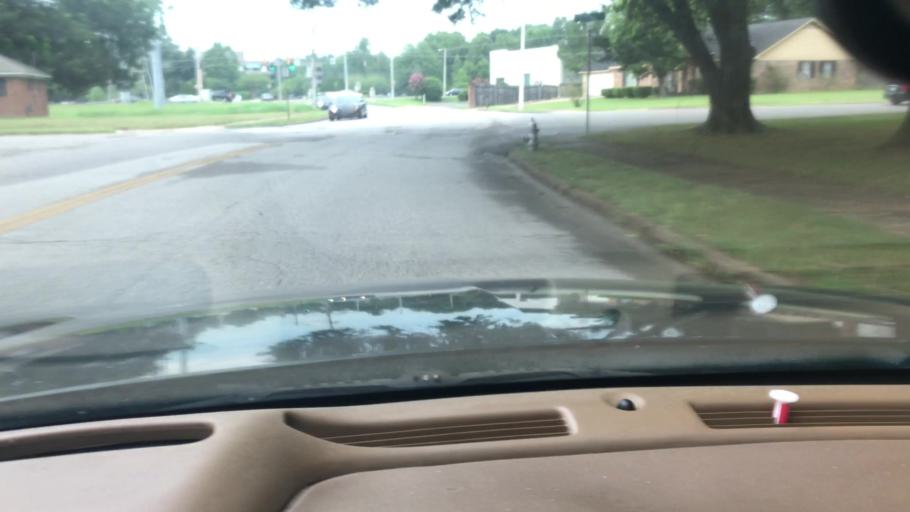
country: US
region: Tennessee
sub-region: Shelby County
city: Germantown
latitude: 35.0738
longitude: -89.8993
